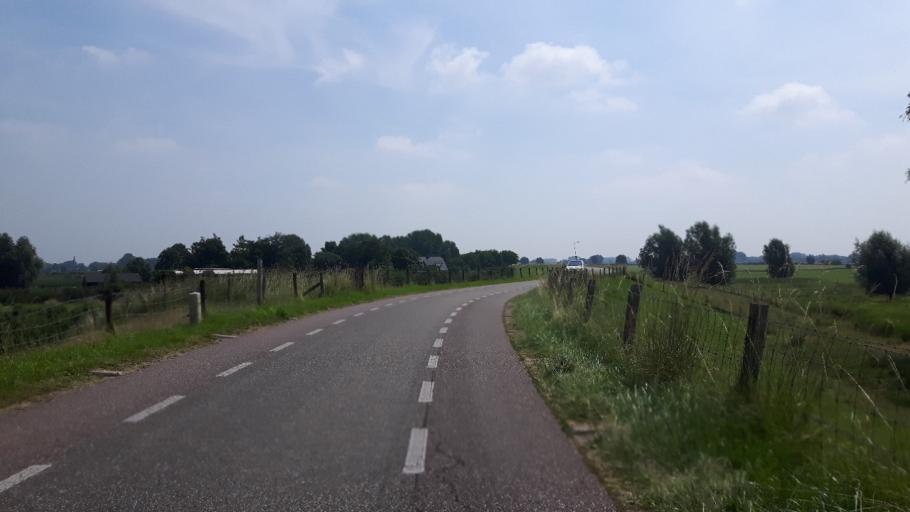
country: NL
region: Utrecht
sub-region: Gemeente Lopik
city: Lopik
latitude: 51.9649
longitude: 4.9543
